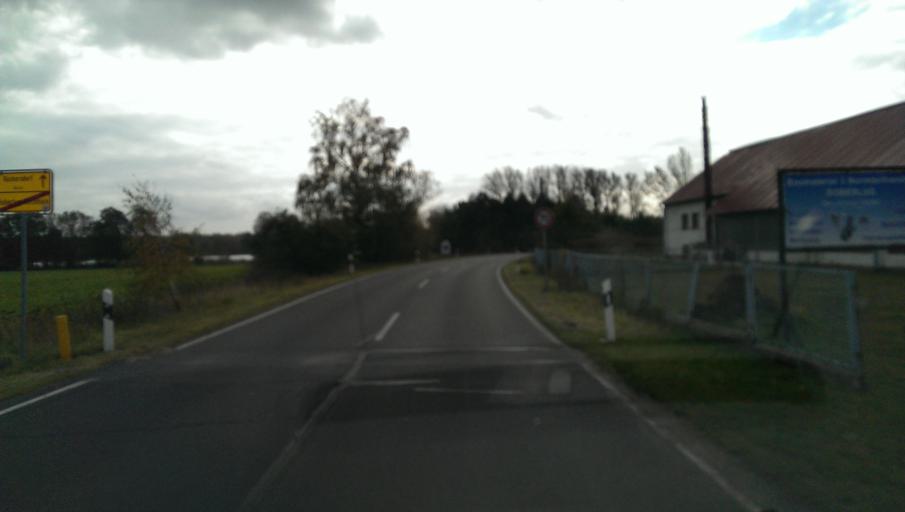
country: DE
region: Brandenburg
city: Ruckersdorf
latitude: 51.6031
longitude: 13.5512
